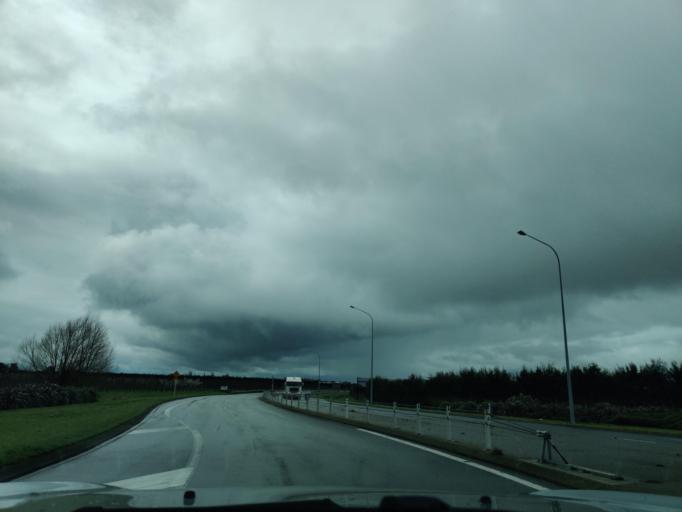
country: NZ
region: Hawke's Bay
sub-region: Hastings District
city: Hastings
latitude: -39.6308
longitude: 176.8012
